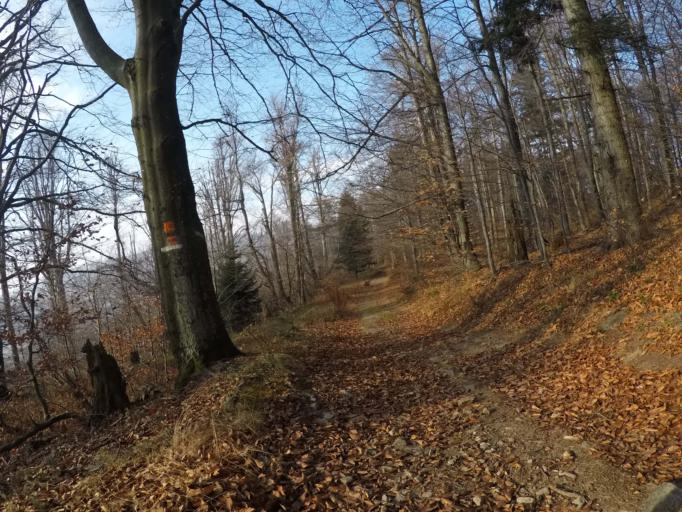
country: SK
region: Kosicky
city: Gelnica
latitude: 48.7630
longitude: 21.0712
